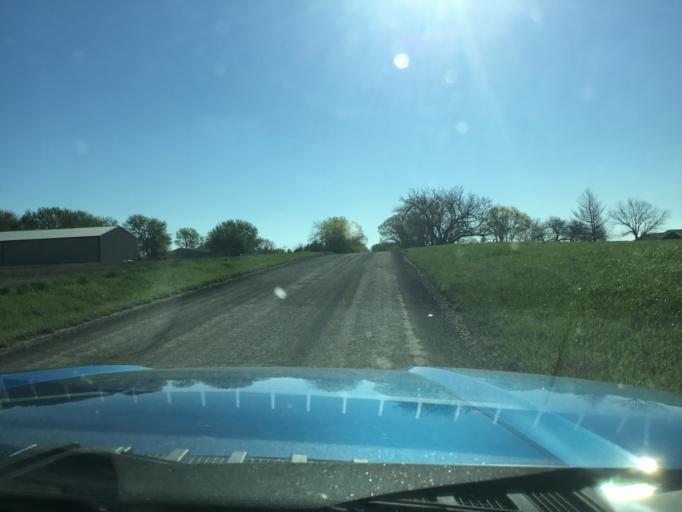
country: US
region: Kansas
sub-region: Douglas County
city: Lawrence
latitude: 38.9568
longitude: -95.3566
